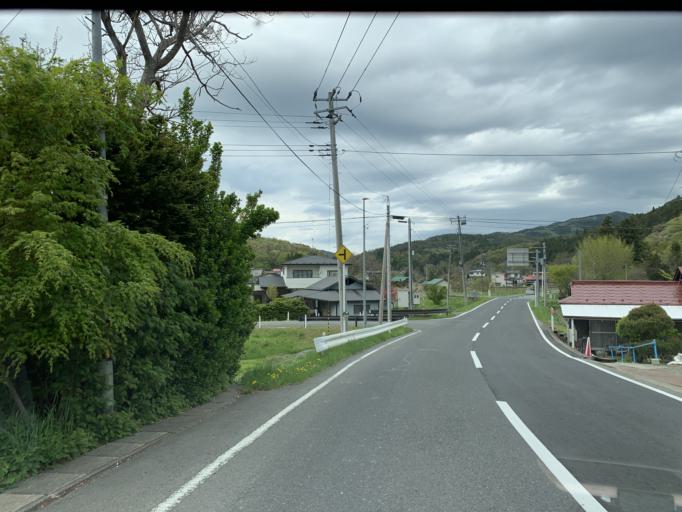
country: JP
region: Iwate
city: Ichinoseki
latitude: 38.7757
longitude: 141.3293
